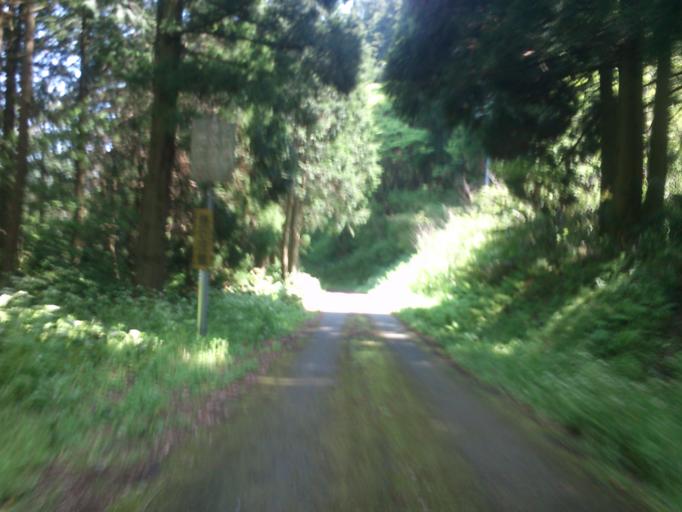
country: JP
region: Kyoto
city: Miyazu
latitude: 35.7125
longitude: 135.1622
